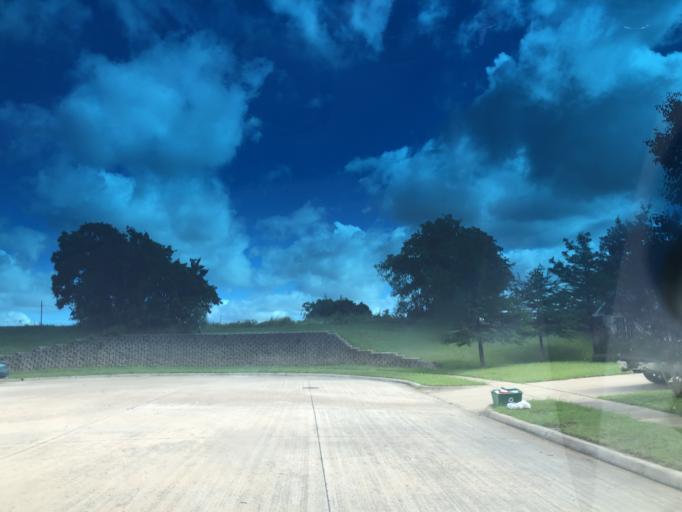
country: US
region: Texas
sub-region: Dallas County
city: Grand Prairie
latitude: 32.6972
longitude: -97.0361
